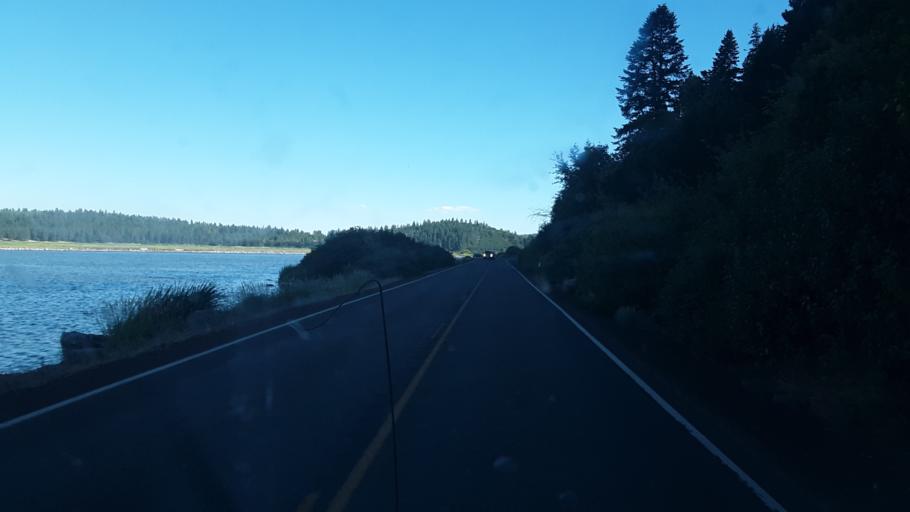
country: US
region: Oregon
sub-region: Klamath County
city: Klamath Falls
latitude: 42.2976
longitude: -121.9322
